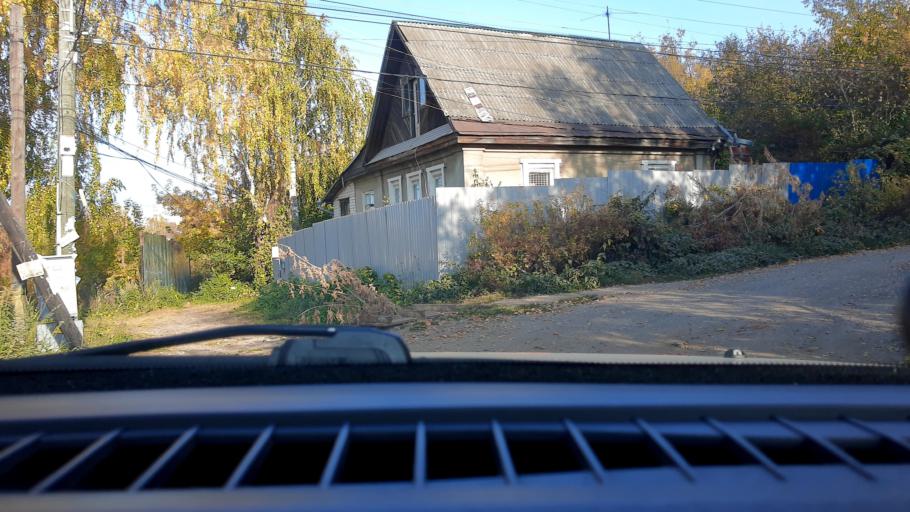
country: RU
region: Nizjnij Novgorod
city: Nizhniy Novgorod
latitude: 56.2521
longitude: 43.9928
